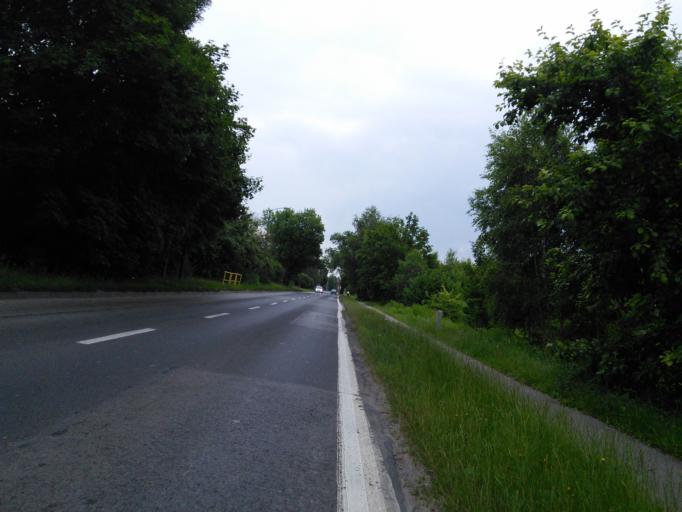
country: PL
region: Silesian Voivodeship
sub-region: Piekary Slaskie
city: Brzeziny Slaskie
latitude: 50.3704
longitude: 18.9663
